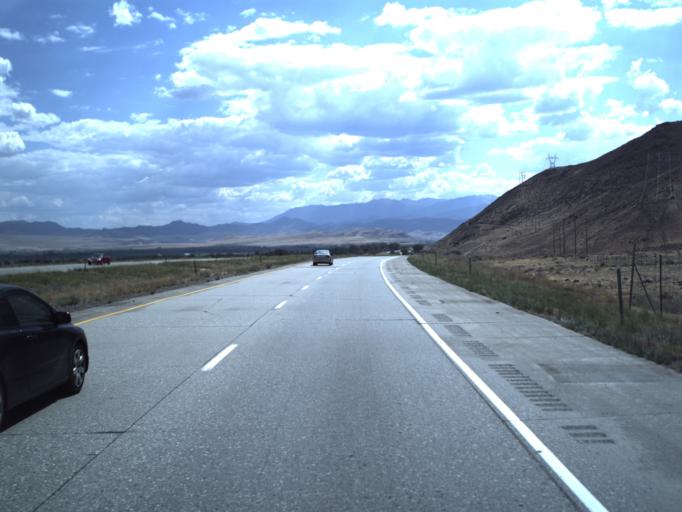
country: US
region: Utah
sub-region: Sevier County
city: Monroe
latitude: 38.7077
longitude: -112.1390
